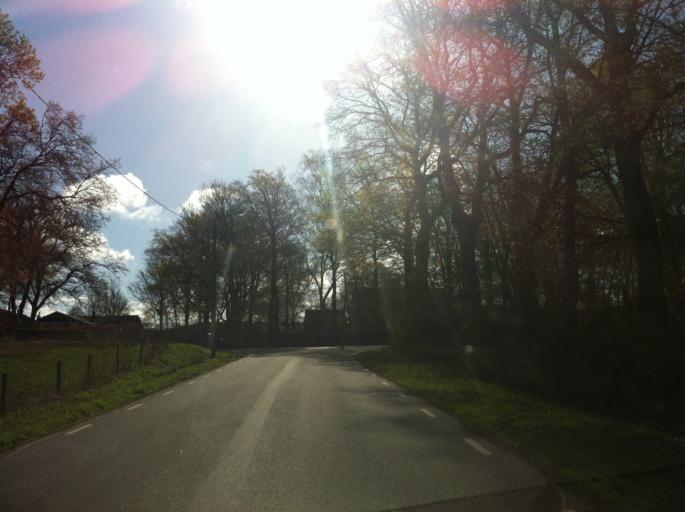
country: SE
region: Skane
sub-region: Eslovs Kommun
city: Stehag
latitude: 55.8991
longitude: 13.4092
